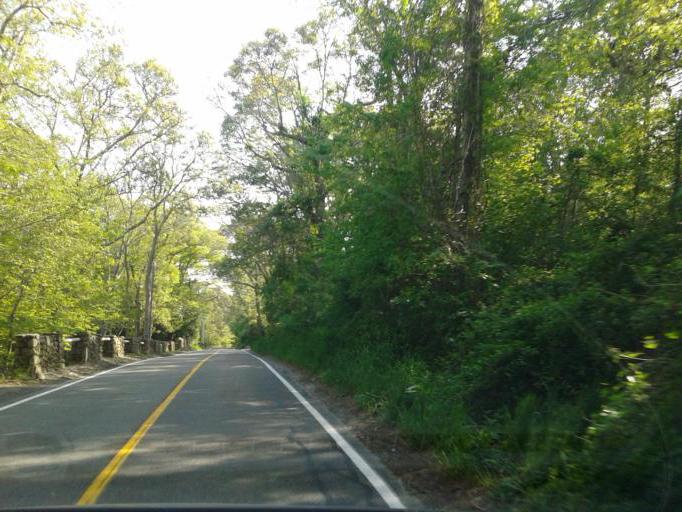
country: US
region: Massachusetts
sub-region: Barnstable County
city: Falmouth
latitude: 41.5311
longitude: -70.6471
